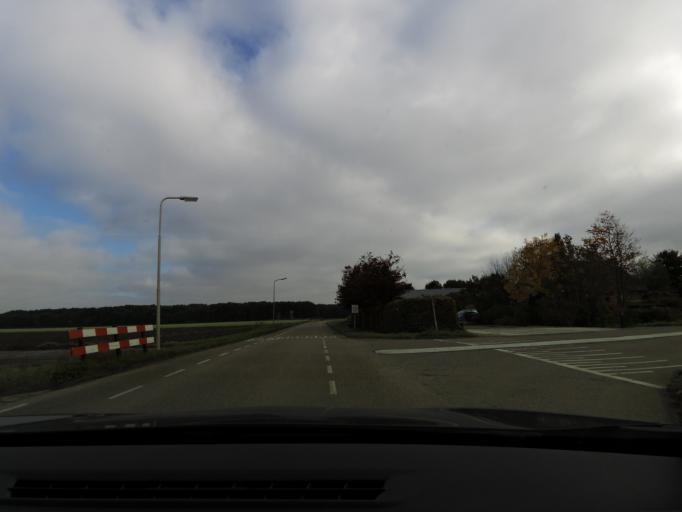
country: NL
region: South Holland
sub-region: Gemeente Oud-Beijerland
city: Oud-Beijerland
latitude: 51.7622
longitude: 4.3652
